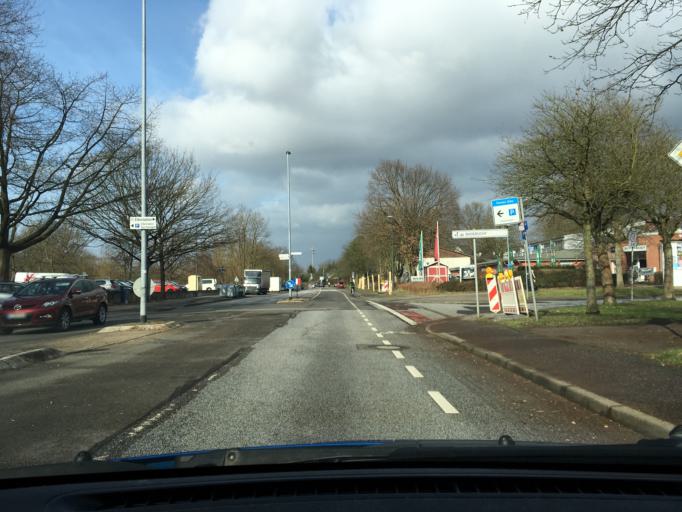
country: DE
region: Schleswig-Holstein
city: Wedel
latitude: 53.5745
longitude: 9.6993
